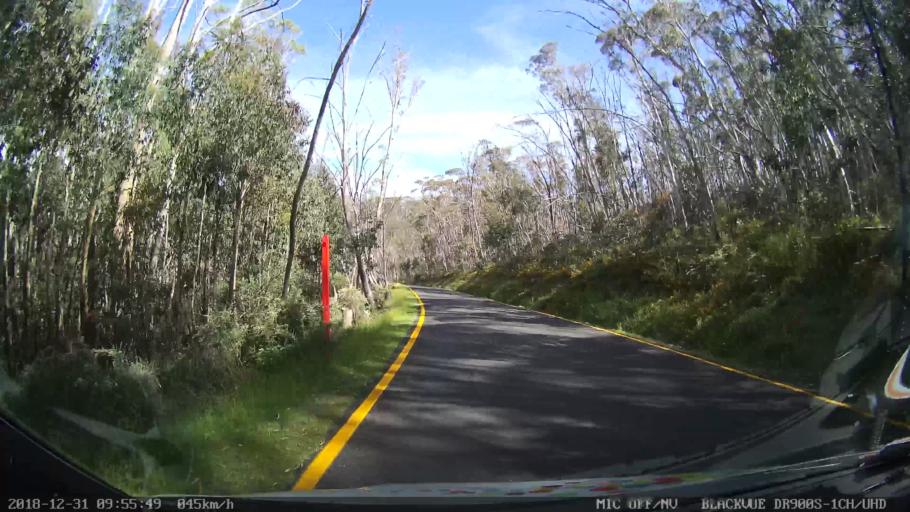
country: AU
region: New South Wales
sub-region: Snowy River
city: Jindabyne
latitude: -36.5316
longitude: 148.2276
